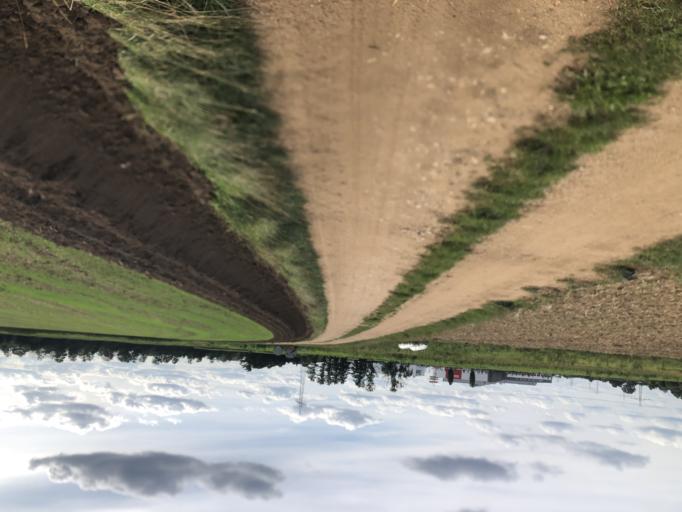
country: DE
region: Bavaria
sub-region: Regierungsbezirk Mittelfranken
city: Furth
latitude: 49.5274
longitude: 10.9968
